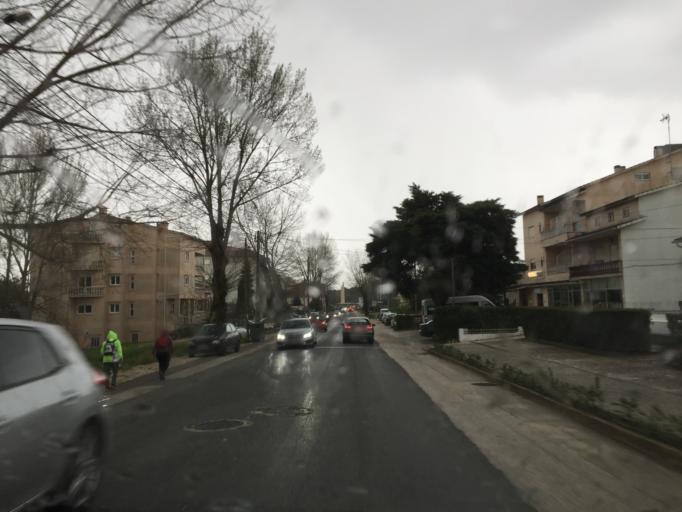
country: PT
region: Santarem
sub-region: Ourem
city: Fatima
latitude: 39.6383
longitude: -8.6846
